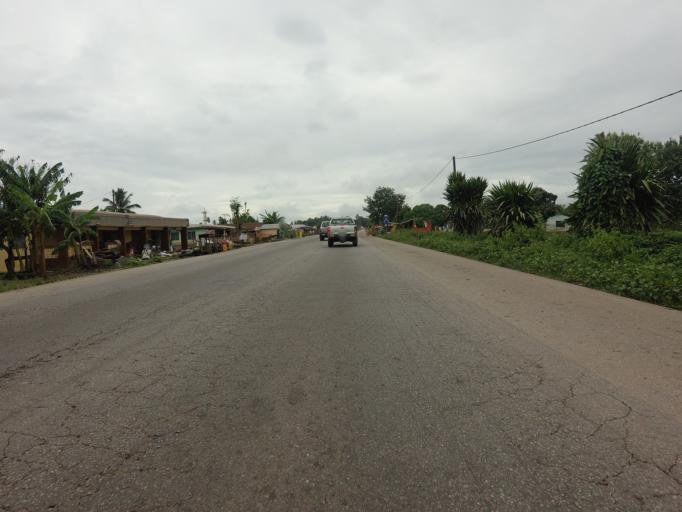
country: GH
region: Eastern
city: Begoro
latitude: 6.4311
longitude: -0.5831
